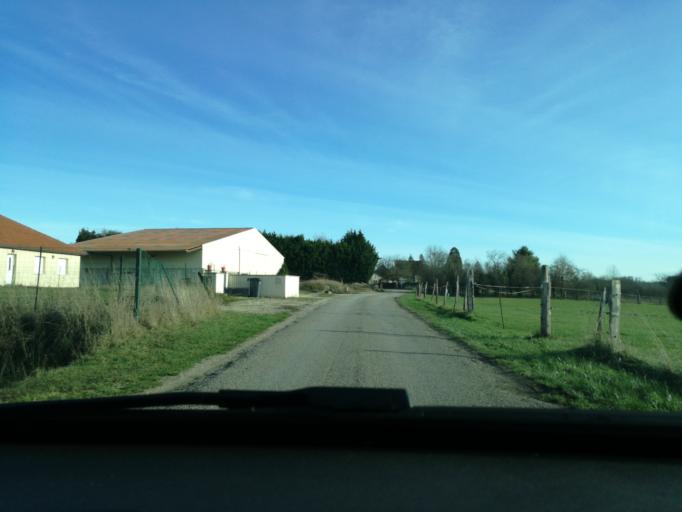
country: FR
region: Lorraine
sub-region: Departement de la Meuse
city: Fains-Veel
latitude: 48.8142
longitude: 5.0789
